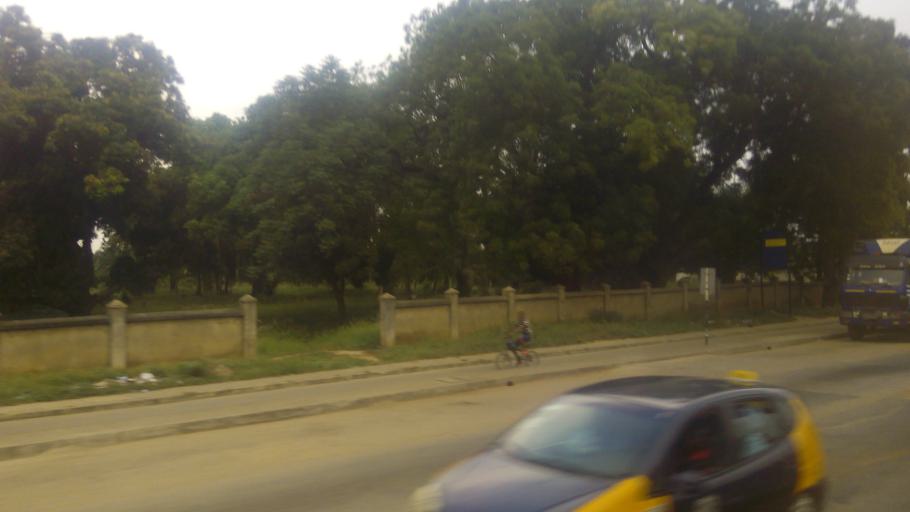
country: GH
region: Western
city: Takoradi
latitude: 4.9061
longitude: -1.7743
